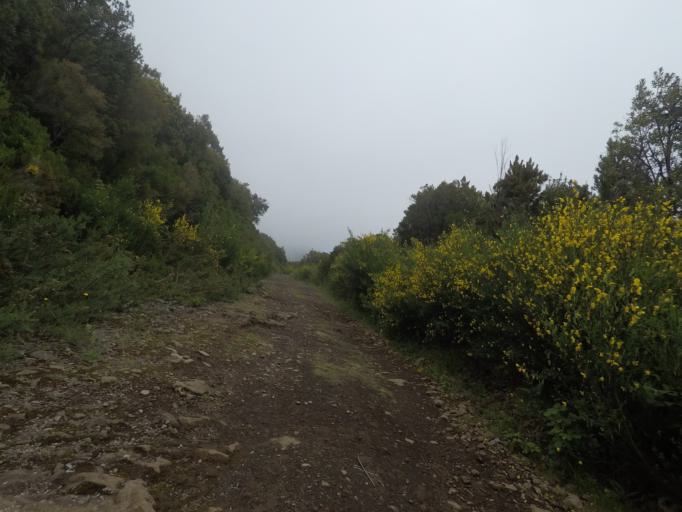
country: PT
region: Madeira
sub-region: Sao Vicente
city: Sao Vicente
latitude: 32.7706
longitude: -17.0560
